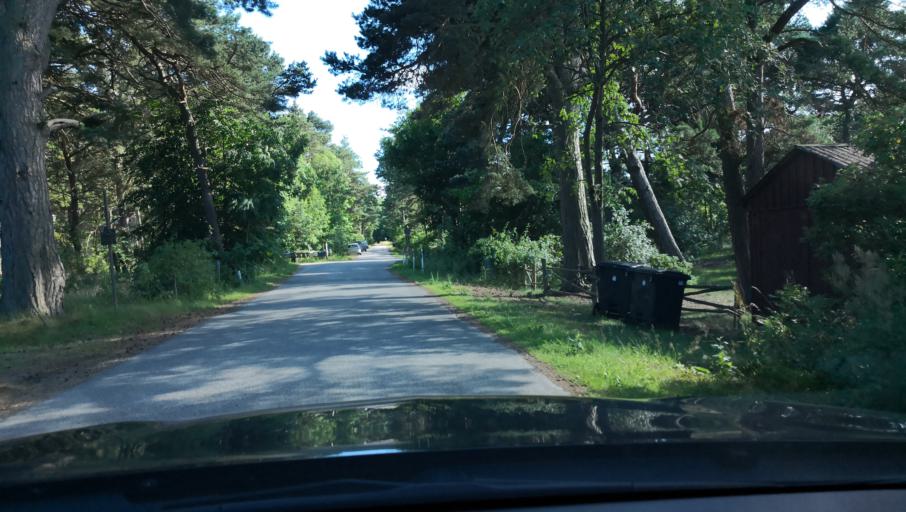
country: SE
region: Skane
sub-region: Simrishamns Kommun
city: Kivik
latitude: 55.7688
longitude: 14.1957
